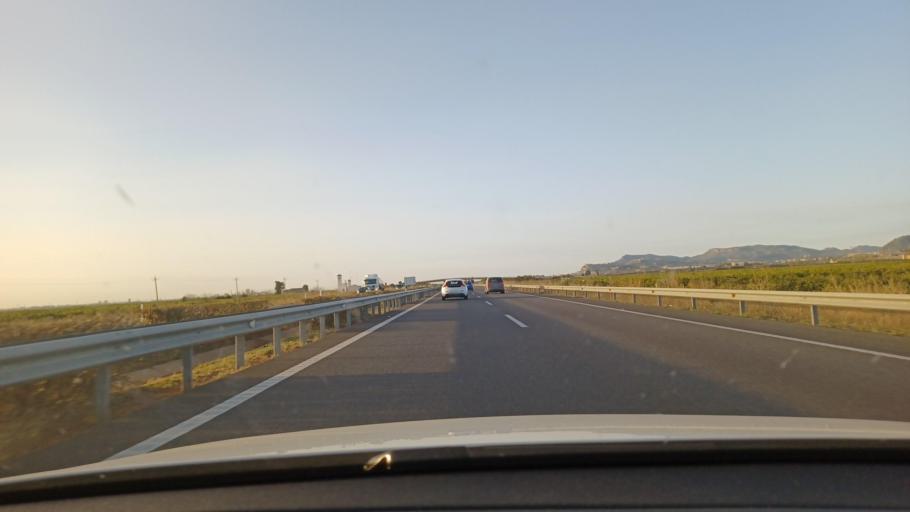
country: ES
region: Valencia
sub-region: Provincia de Valencia
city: Faura
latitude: 39.7161
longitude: -0.2367
